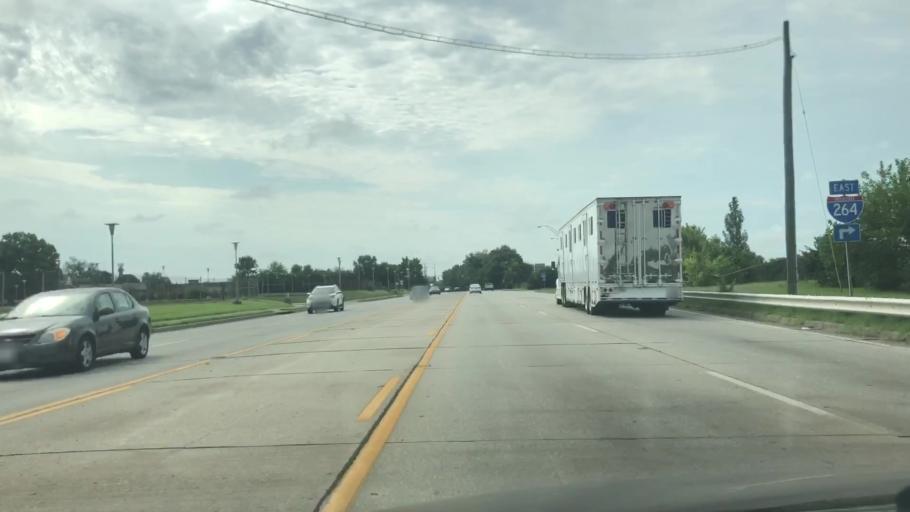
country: US
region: Kentucky
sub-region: Jefferson County
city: Audubon Park
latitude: 38.1889
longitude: -85.7260
